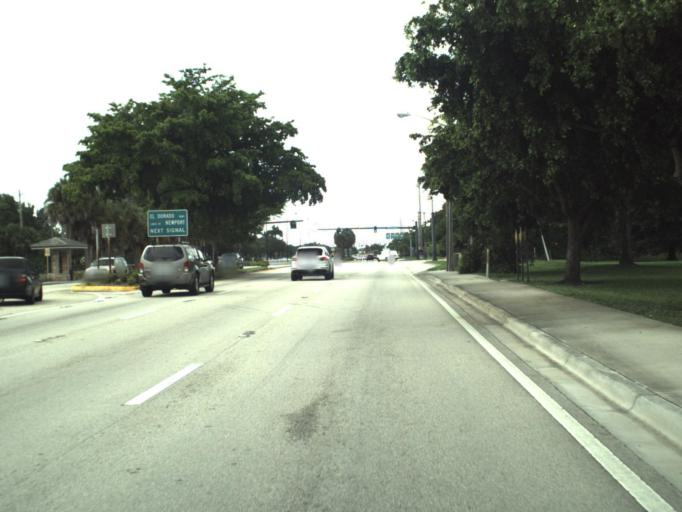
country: US
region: Florida
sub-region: Broward County
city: Plantation
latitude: 26.1210
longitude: -80.2471
